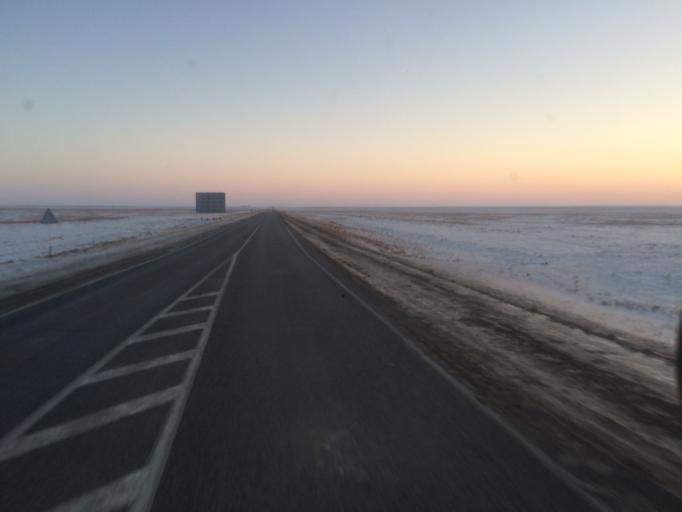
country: KZ
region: Qyzylorda
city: Sekseuil
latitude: 47.4792
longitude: 61.5358
